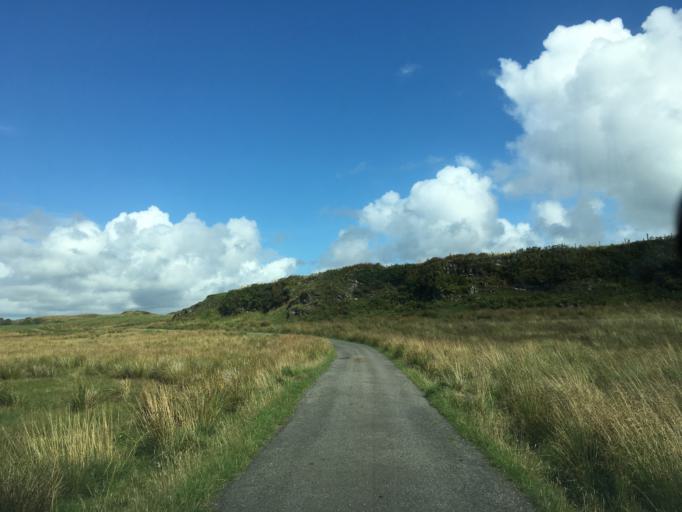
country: GB
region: Scotland
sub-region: Argyll and Bute
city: Isle Of Mull
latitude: 56.2191
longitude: -5.6503
